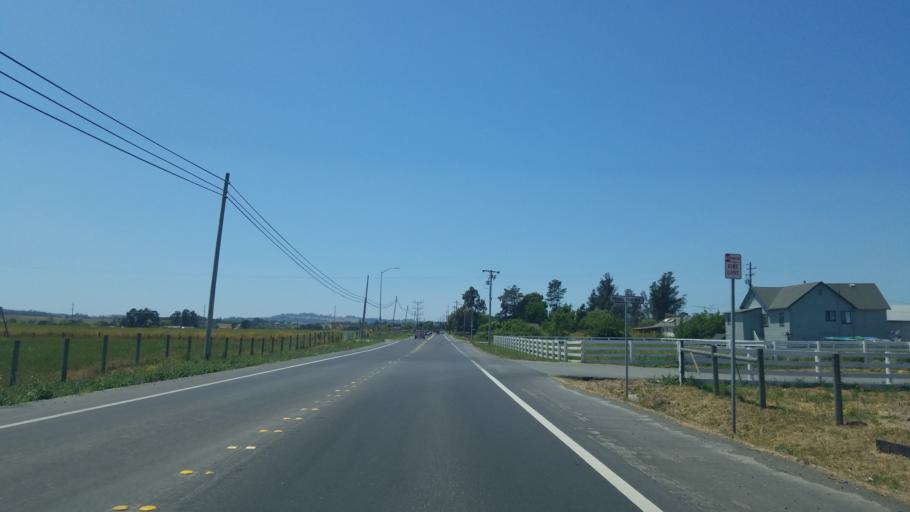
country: US
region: California
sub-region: Sonoma County
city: Rohnert Park
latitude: 38.3633
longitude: -122.7360
